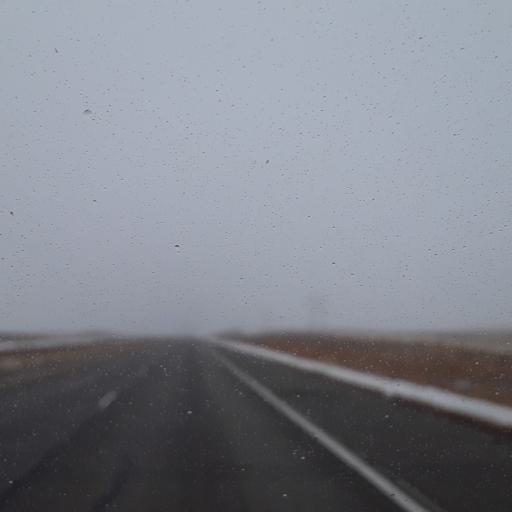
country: US
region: Colorado
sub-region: Logan County
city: Sterling
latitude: 40.7825
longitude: -102.9098
